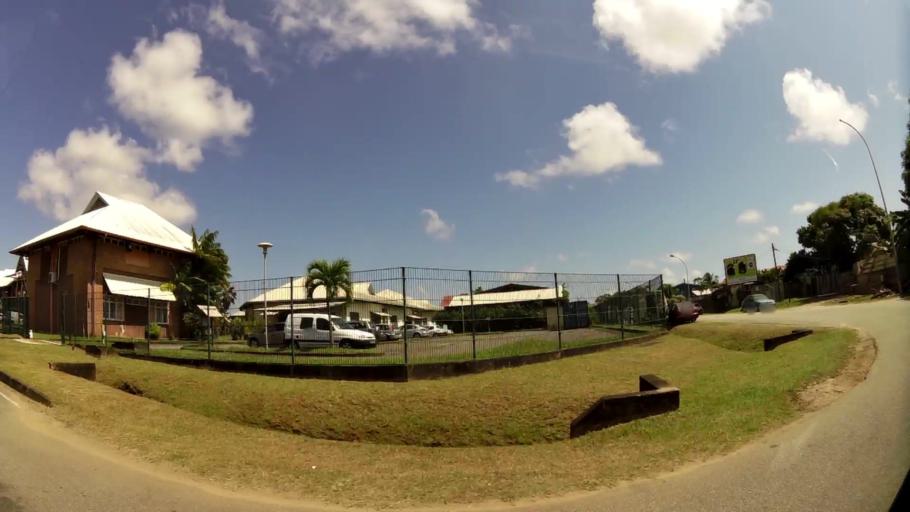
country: GF
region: Guyane
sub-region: Guyane
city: Cayenne
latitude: 4.9292
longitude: -52.3270
